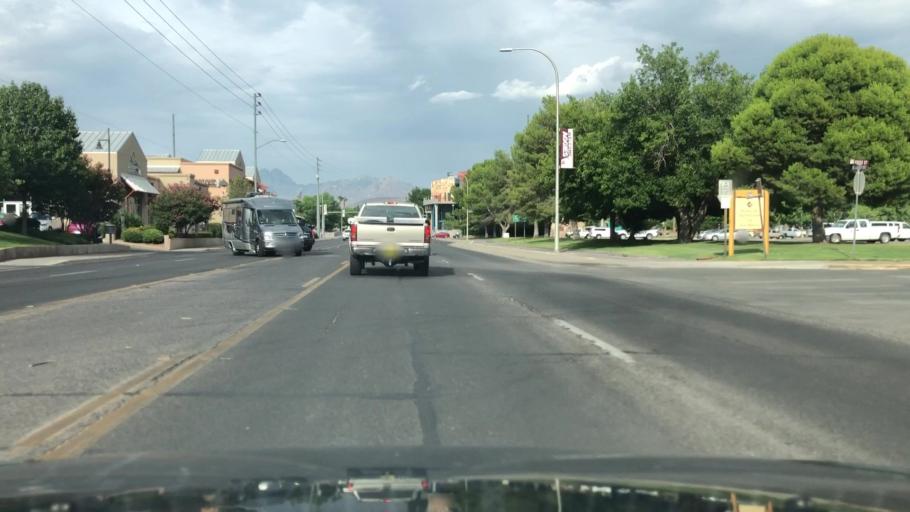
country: US
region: New Mexico
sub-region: Dona Ana County
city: University Park
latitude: 32.2836
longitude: -106.7585
